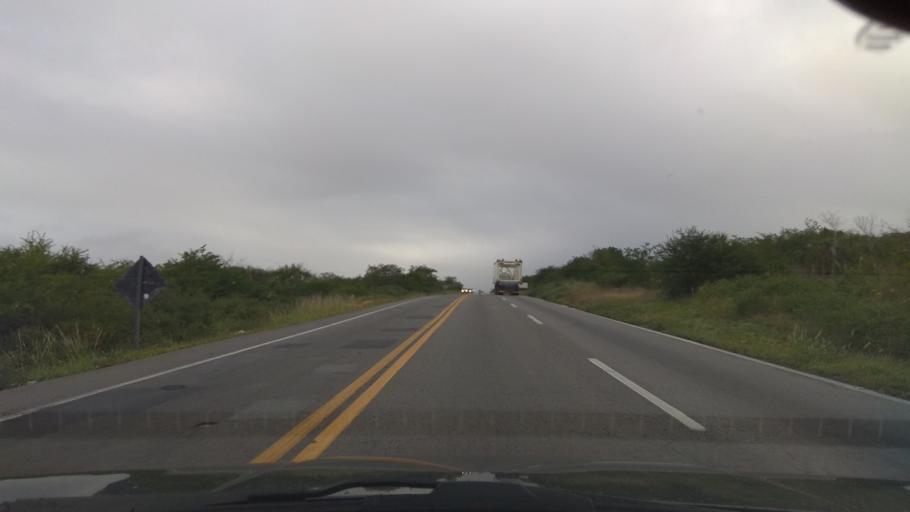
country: BR
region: Bahia
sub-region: Santa Ines
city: Santa Ines
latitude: -13.0284
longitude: -39.9618
